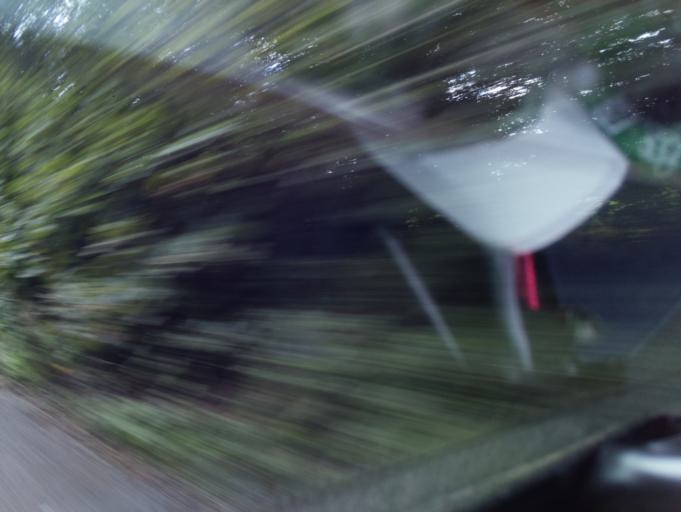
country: GB
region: England
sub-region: Devon
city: Modbury
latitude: 50.3387
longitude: -3.8582
